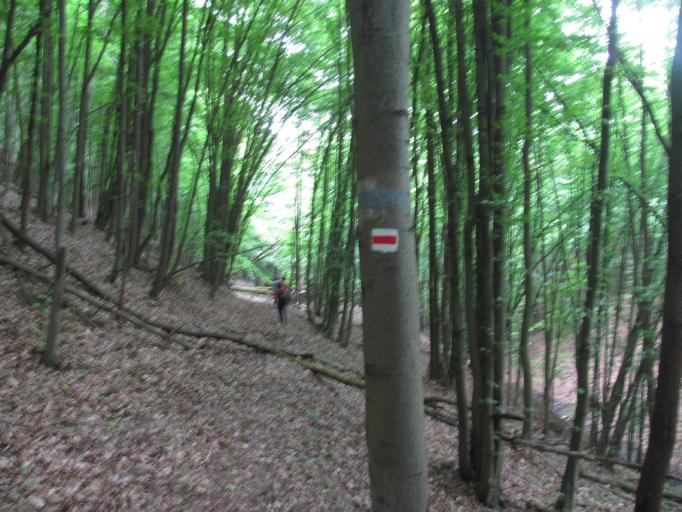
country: HU
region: Borsod-Abauj-Zemplen
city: Jardanhaza
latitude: 48.1793
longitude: 20.1579
